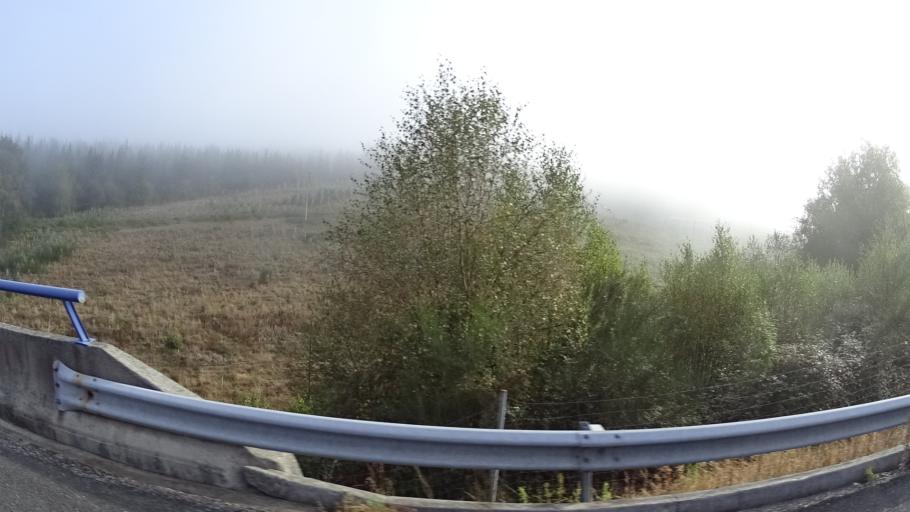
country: ES
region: Galicia
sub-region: Provincia de Lugo
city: Lancara
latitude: 42.9228
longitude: -7.3556
